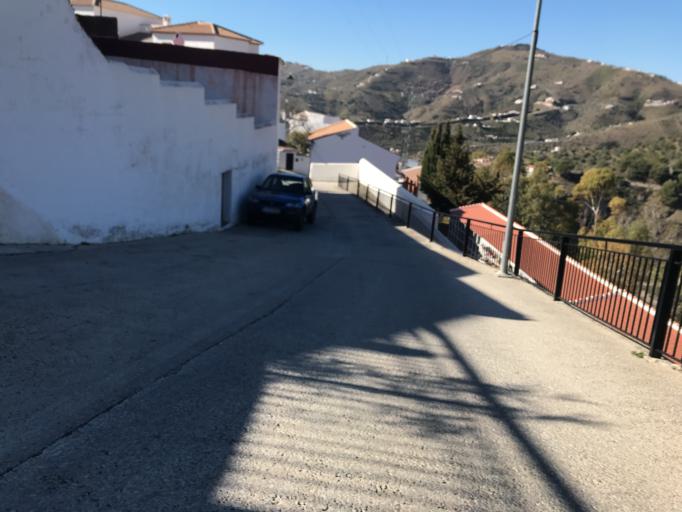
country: ES
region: Andalusia
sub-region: Provincia de Malaga
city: Canillas de Albaida
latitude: 36.8474
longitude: -3.9879
